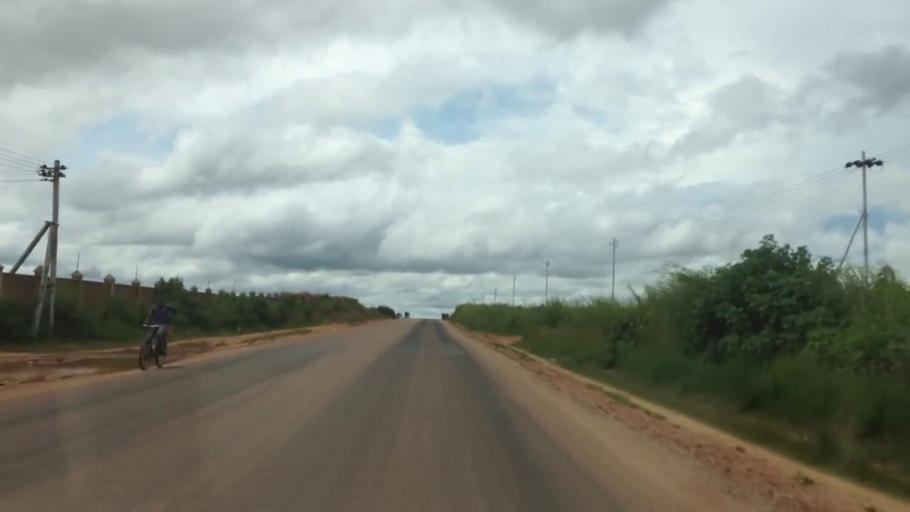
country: CD
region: Katanga
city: Kolwezi
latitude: -10.7461
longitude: 25.5138
